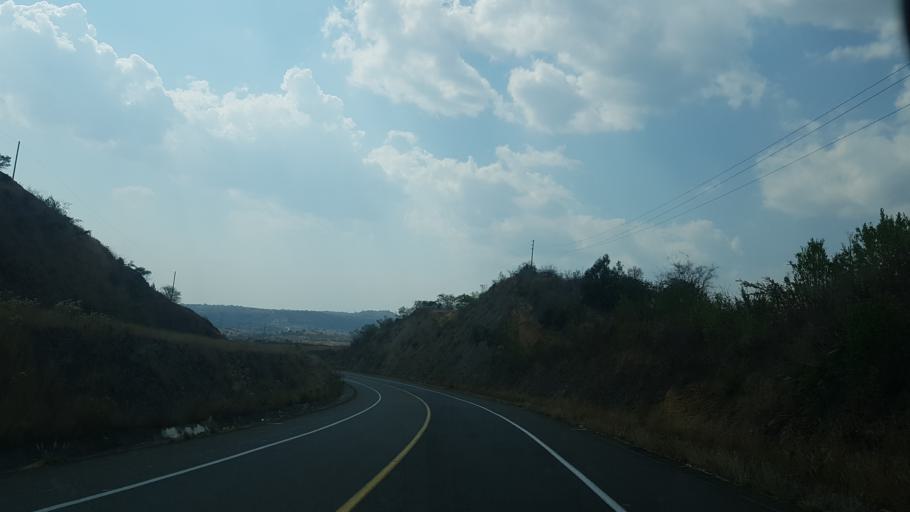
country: MX
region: Puebla
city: San Juan Amecac
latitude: 18.8215
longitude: -98.6848
